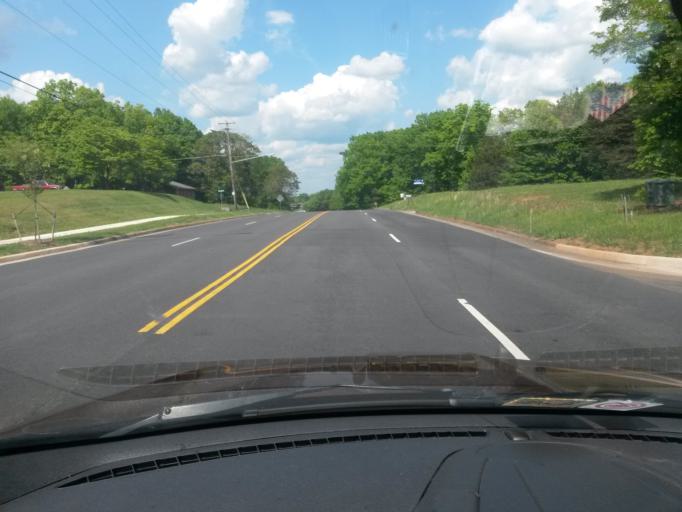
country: US
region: Virginia
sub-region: Campbell County
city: Timberlake
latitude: 37.3352
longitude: -79.2133
